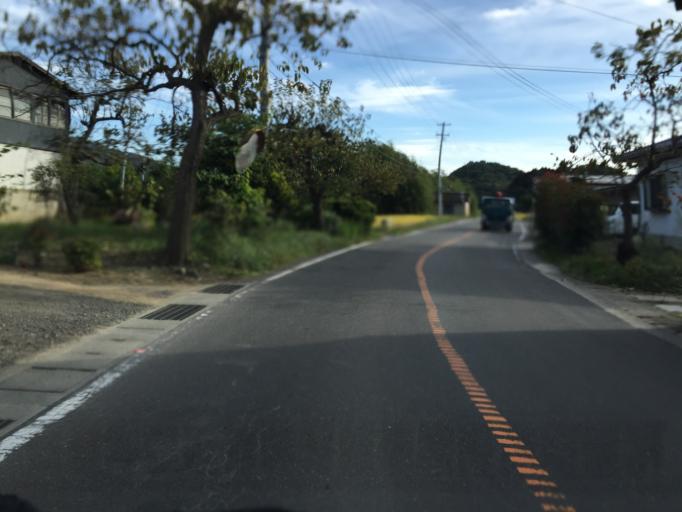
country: JP
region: Fukushima
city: Yanagawamachi-saiwaicho
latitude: 37.8439
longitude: 140.6150
